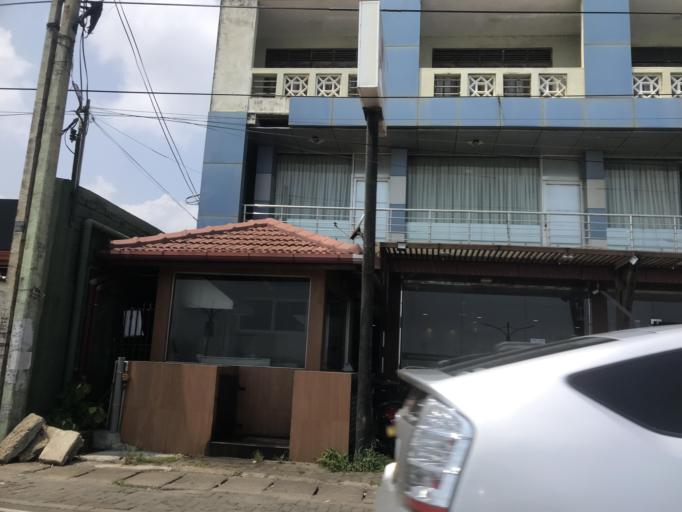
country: LK
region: Southern
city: Matara
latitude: 5.9427
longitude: 80.5538
